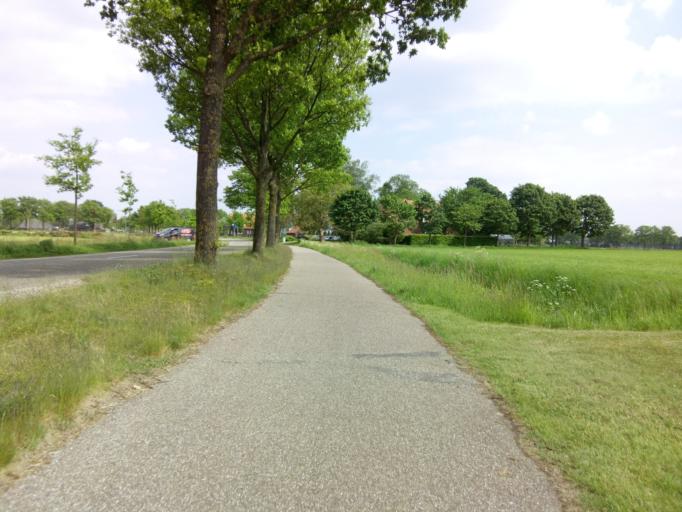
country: NL
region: Gelderland
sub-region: Oost Gelre
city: Lichtenvoorde
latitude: 52.0540
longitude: 6.5832
